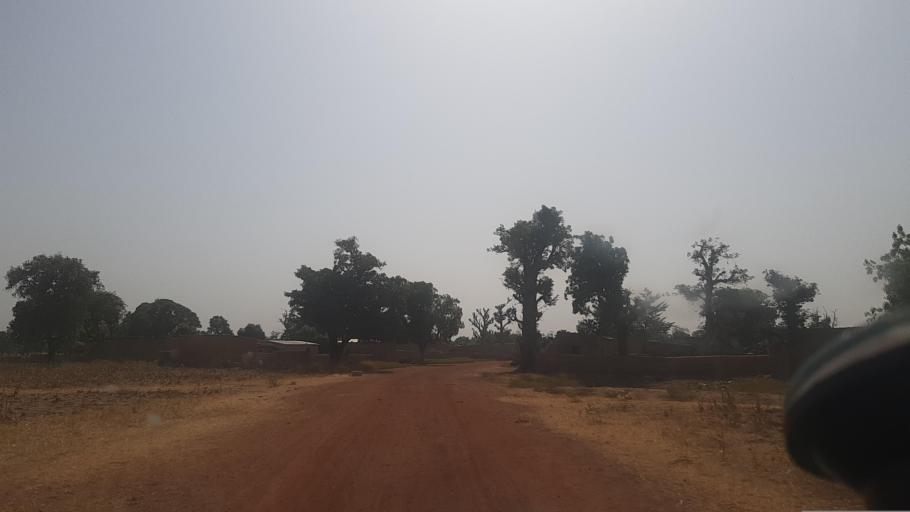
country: ML
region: Segou
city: Baroueli
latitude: 13.0142
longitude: -6.4235
